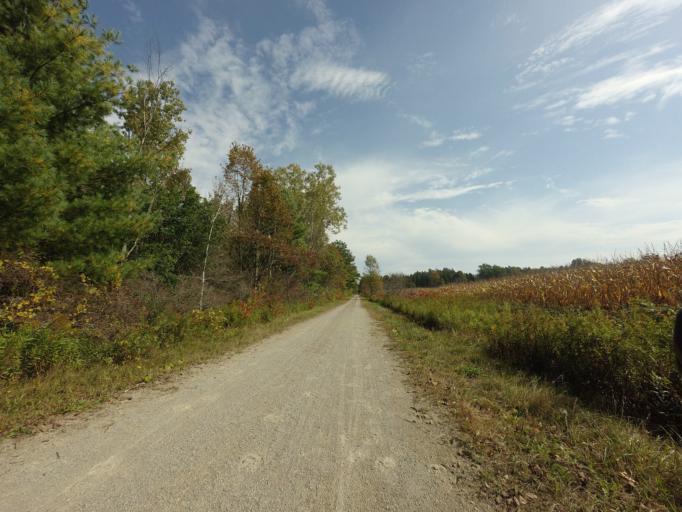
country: CA
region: Ontario
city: Brantford
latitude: 43.1828
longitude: -80.1595
